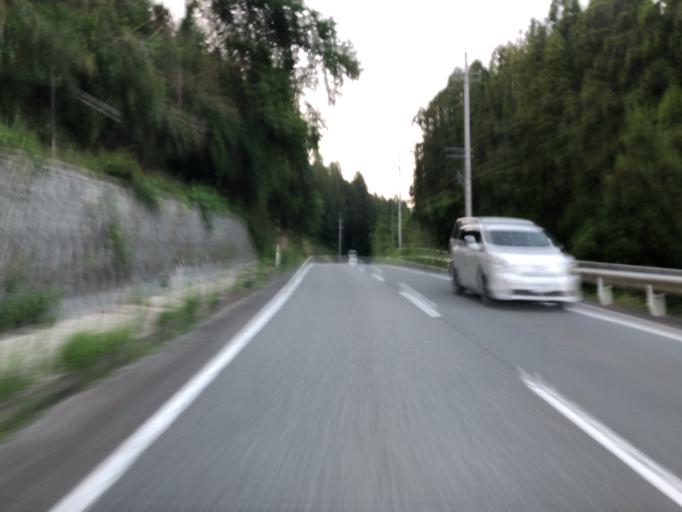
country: JP
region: Fukushima
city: Namie
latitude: 37.2712
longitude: 140.9767
